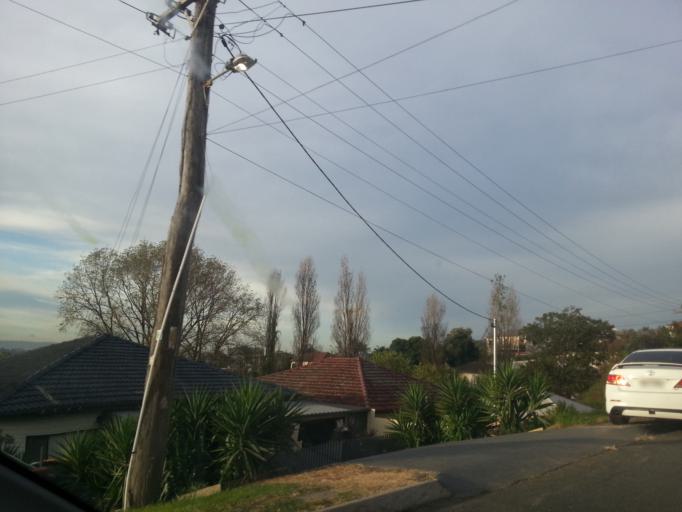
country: AU
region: New South Wales
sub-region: Wollongong
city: Lake Heights
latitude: -34.4772
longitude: 150.8712
